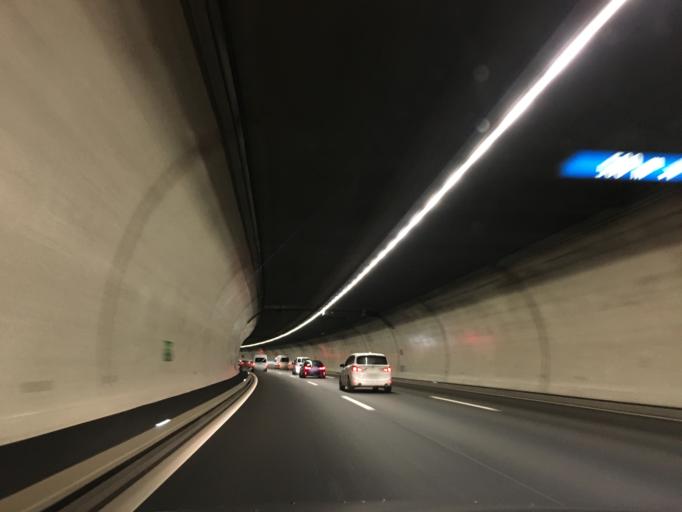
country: CH
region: Zurich
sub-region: Bezirk Affoltern
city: Wettswil / Wettswil (Dorf)
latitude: 47.3444
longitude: 8.4765
